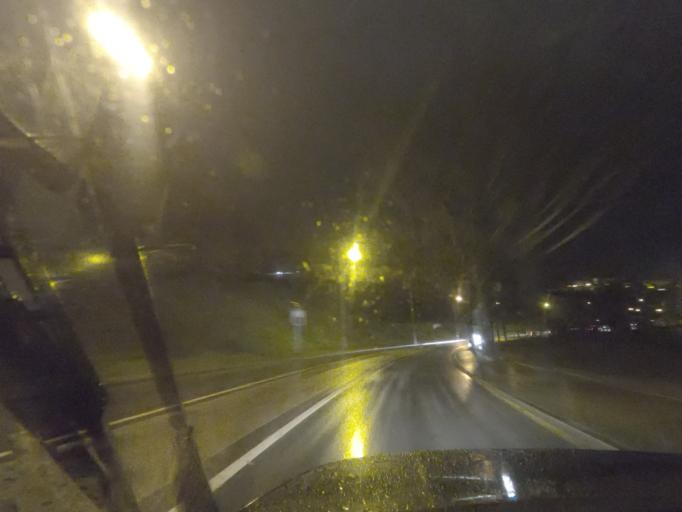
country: PT
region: Vila Real
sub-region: Vila Real
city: Vila Real
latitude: 41.3065
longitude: -7.7368
